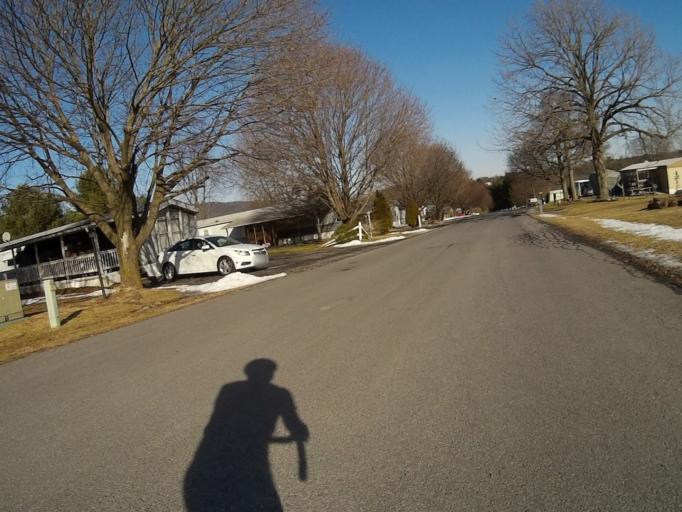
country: US
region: Pennsylvania
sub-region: Centre County
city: Houserville
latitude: 40.8713
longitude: -77.8639
